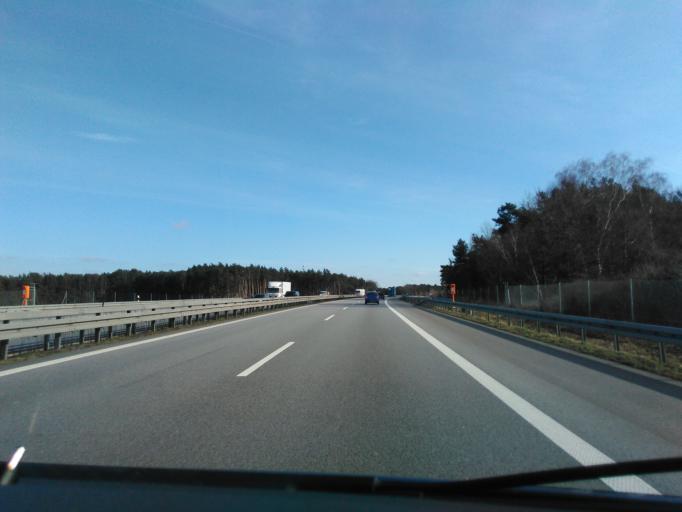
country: DE
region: Brandenburg
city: Luebben
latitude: 51.8786
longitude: 13.8835
